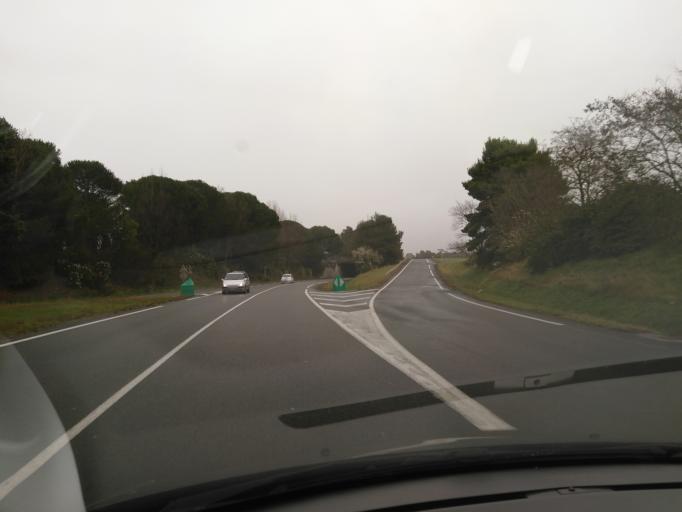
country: FR
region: Languedoc-Roussillon
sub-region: Departement de l'Aude
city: Pennautier
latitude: 43.2114
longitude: 2.3132
